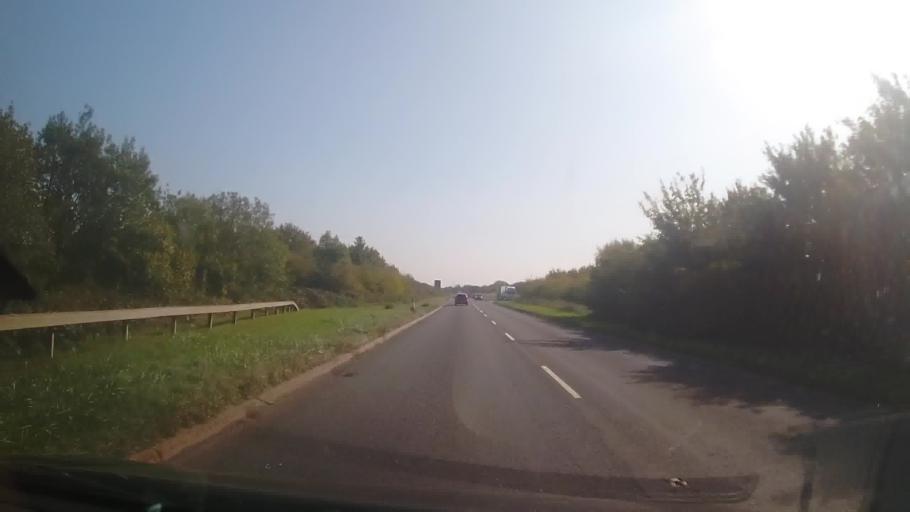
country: GB
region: England
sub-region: Worcestershire
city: Pershore
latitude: 52.1300
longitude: -2.0529
